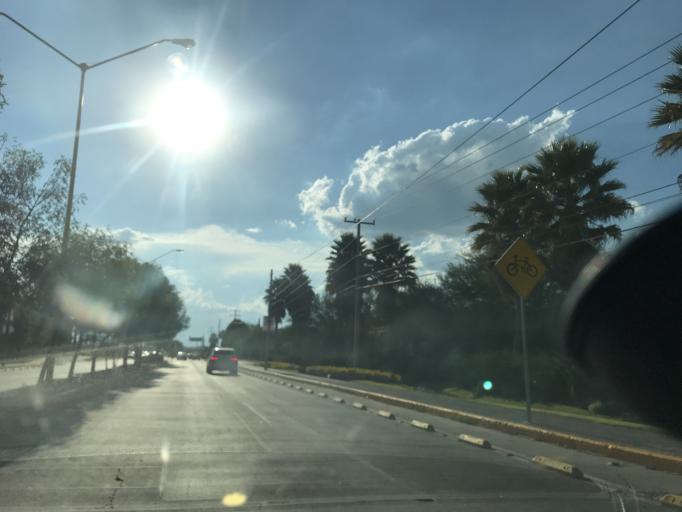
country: MX
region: Aguascalientes
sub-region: Aguascalientes
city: Pocitos
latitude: 21.9097
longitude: -102.3234
